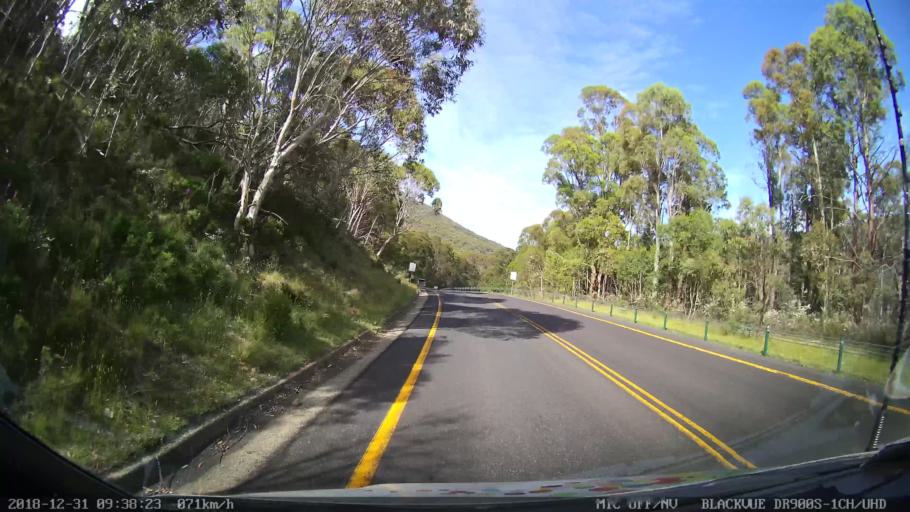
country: AU
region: New South Wales
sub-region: Snowy River
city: Jindabyne
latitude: -36.4738
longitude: 148.3682
